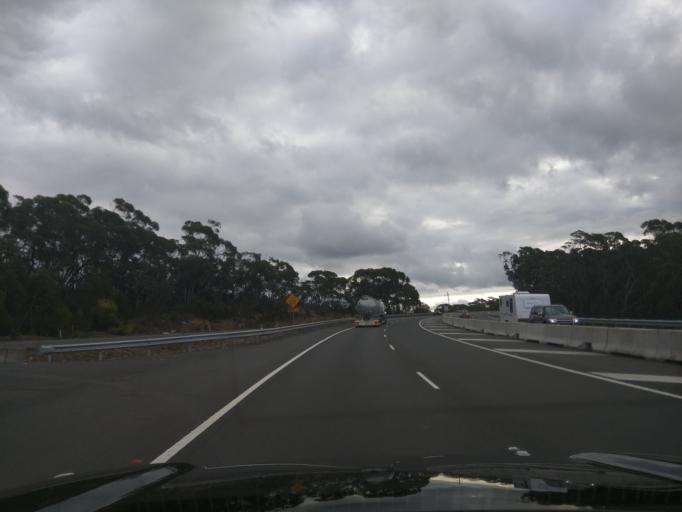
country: AU
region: New South Wales
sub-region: Wollongong
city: Mount Keira
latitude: -34.3611
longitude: 150.8151
